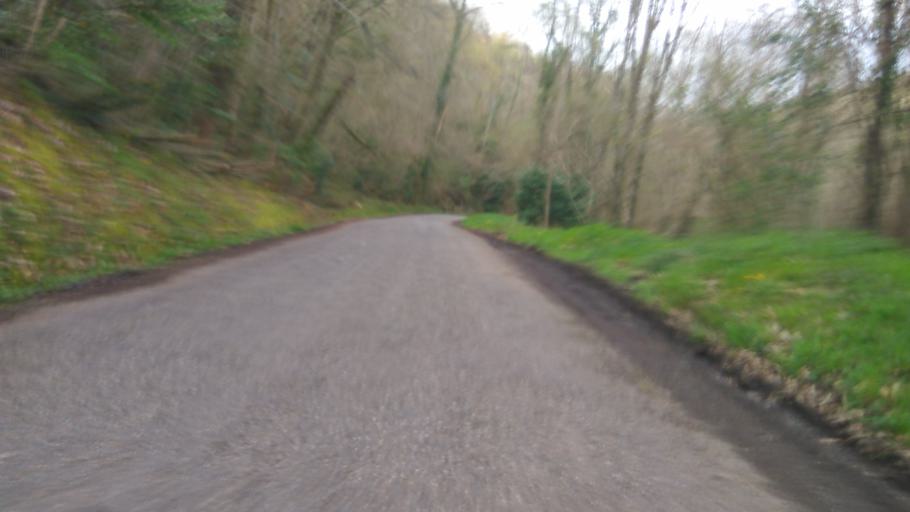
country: FR
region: Aquitaine
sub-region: Departement des Pyrenees-Atlantiques
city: Mazeres-Lezons
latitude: 43.2681
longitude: -0.3578
